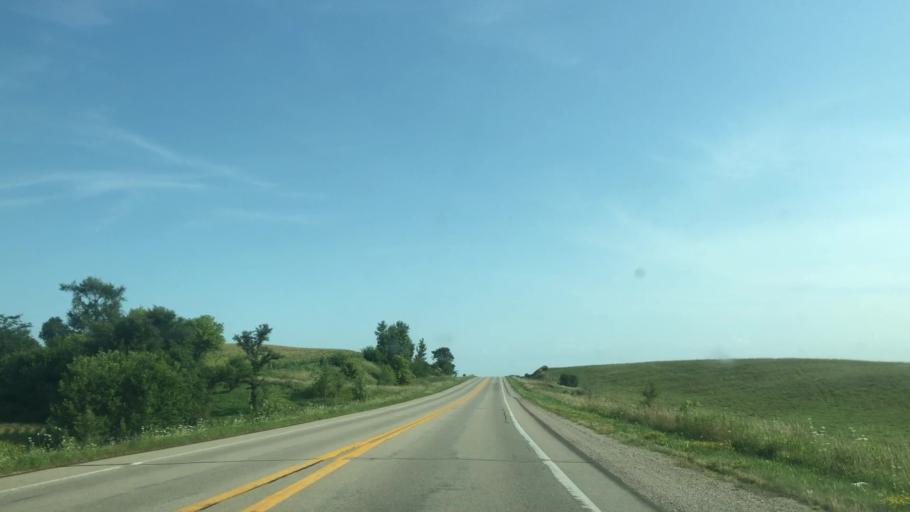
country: US
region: Iowa
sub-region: Marshall County
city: Marshalltown
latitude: 42.0465
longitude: -93.0002
